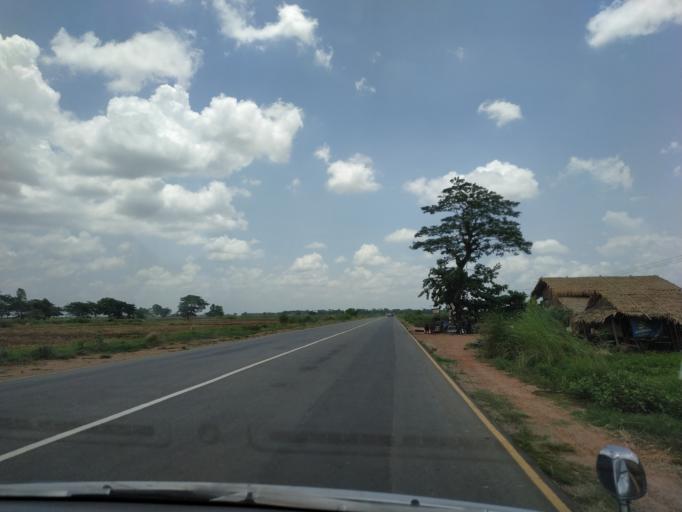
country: MM
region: Bago
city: Bago
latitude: 17.4688
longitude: 96.5678
